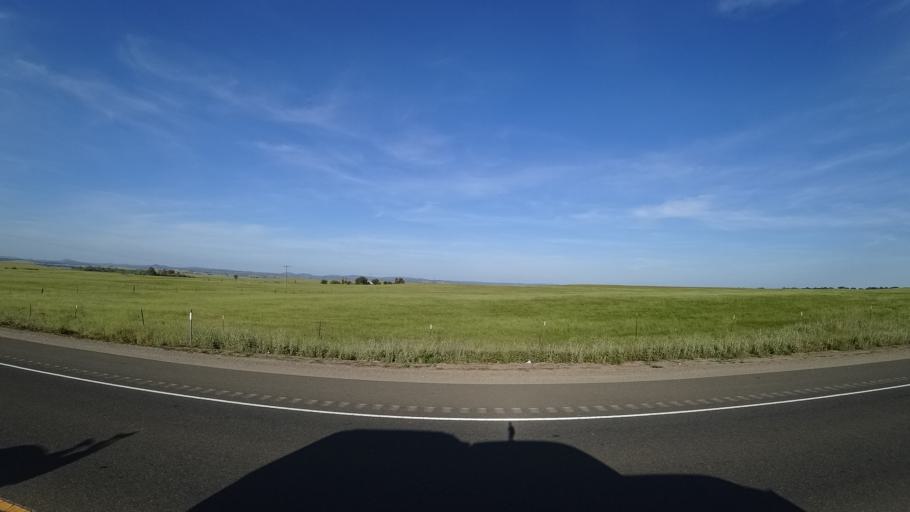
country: US
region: California
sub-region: Placer County
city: Sheridan
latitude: 38.9527
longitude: -121.3561
